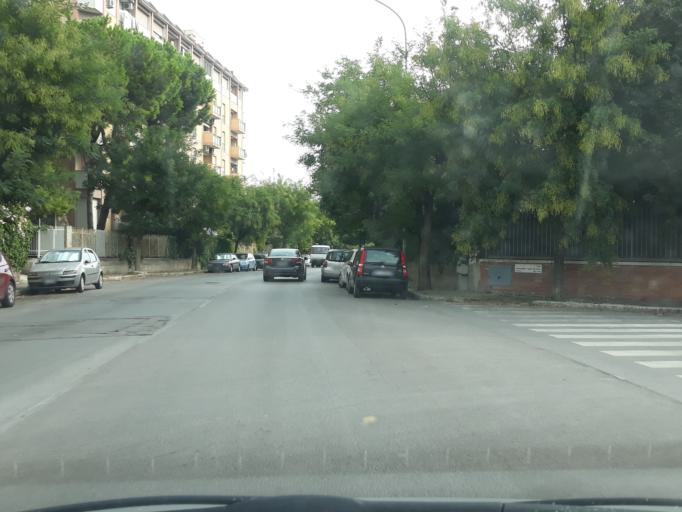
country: IT
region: Sicily
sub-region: Palermo
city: Palermo
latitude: 38.1009
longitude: 13.3274
